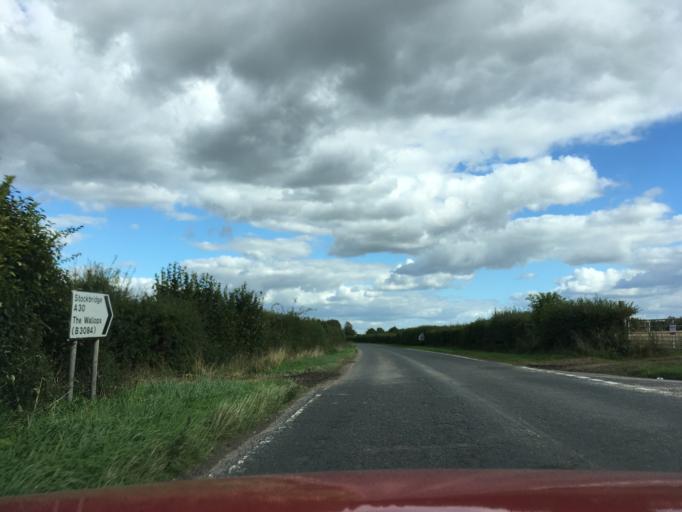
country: GB
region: England
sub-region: Hampshire
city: East Dean
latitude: 51.1116
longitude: -1.5930
